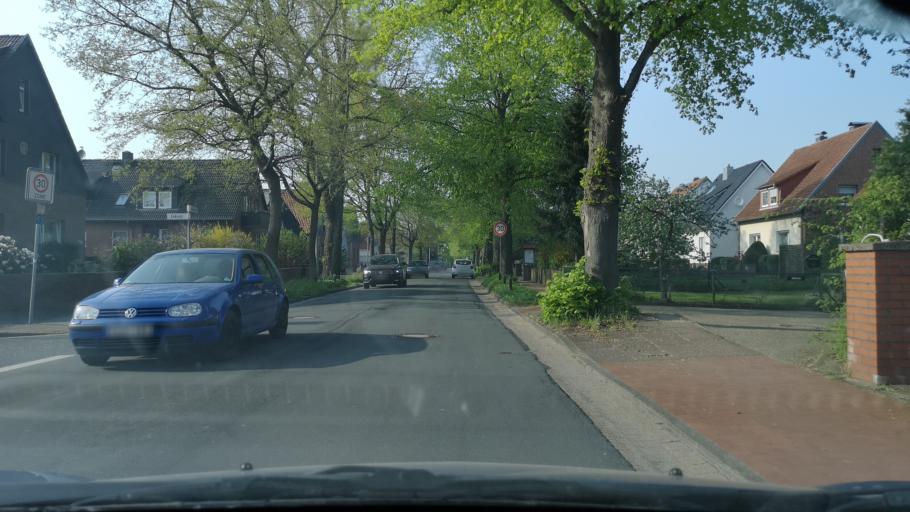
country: DE
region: Lower Saxony
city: Garbsen-Mitte
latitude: 52.4439
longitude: 9.6689
